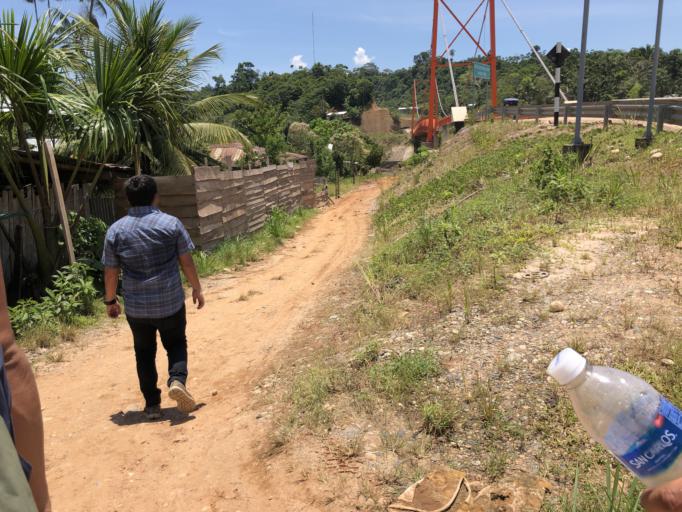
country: PE
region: Loreto
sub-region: Datem Del Maranon
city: Saramiriza
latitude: -4.6046
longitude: -77.8665
